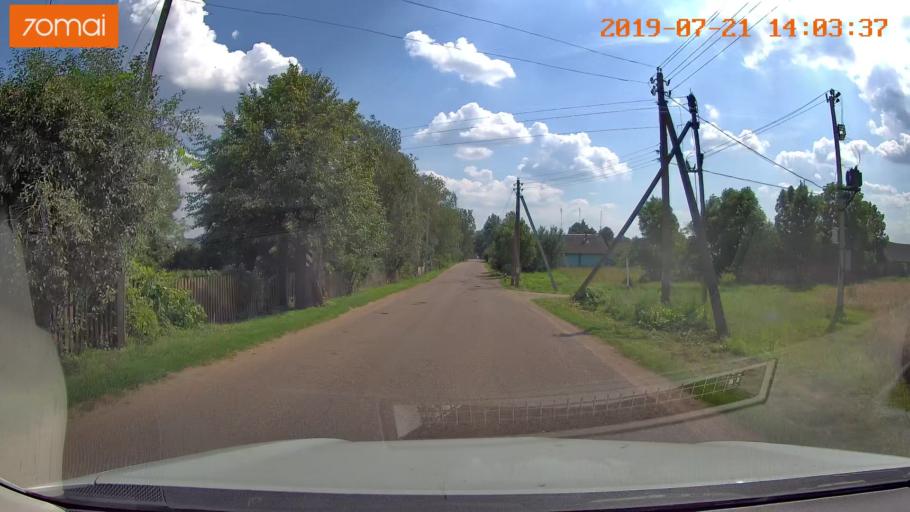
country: BY
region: Grodnenskaya
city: Lyubcha
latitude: 53.7276
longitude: 26.0924
